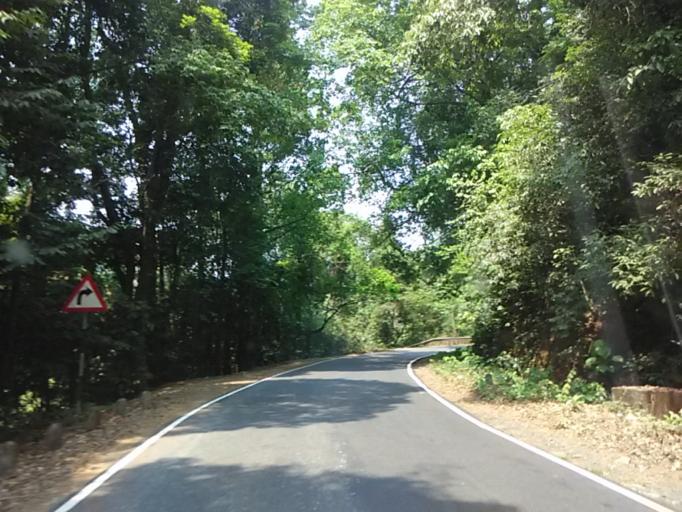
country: IN
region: Karnataka
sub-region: Kodagu
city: Virarajendrapet
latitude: 12.0993
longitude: 75.7566
